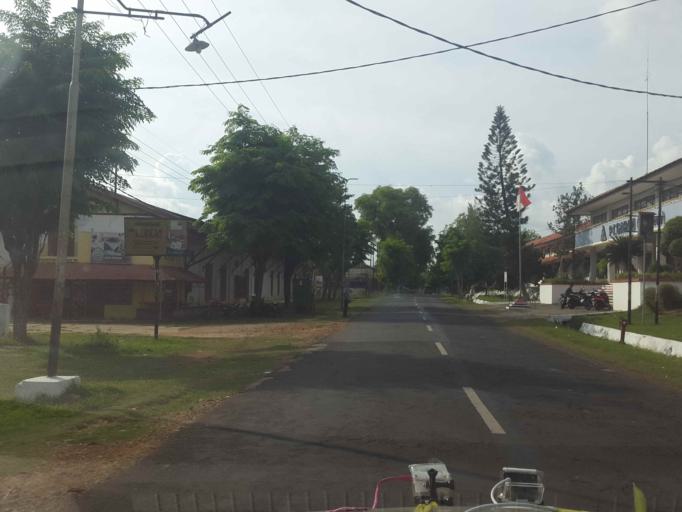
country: ID
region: East Java
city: Kalianget
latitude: -7.0528
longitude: 113.9364
